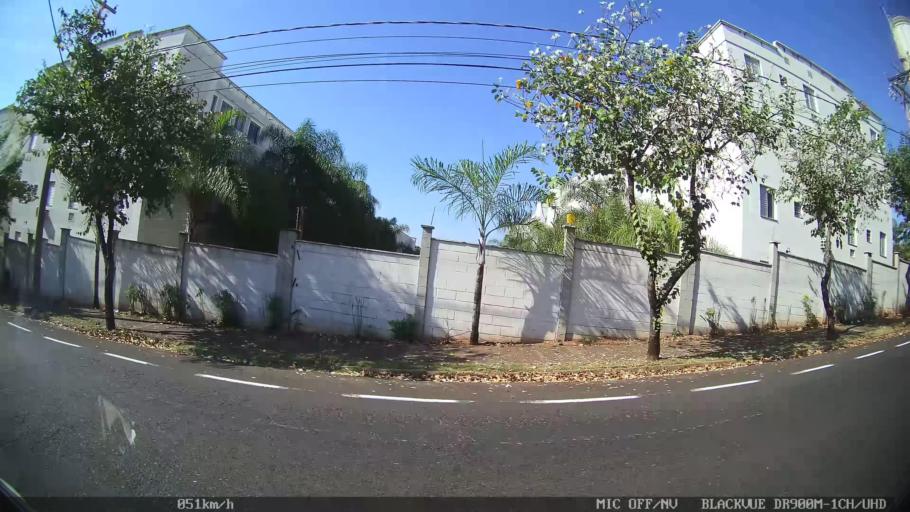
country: BR
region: Sao Paulo
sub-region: Sao Jose Do Rio Preto
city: Sao Jose do Rio Preto
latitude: -20.7765
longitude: -49.3989
